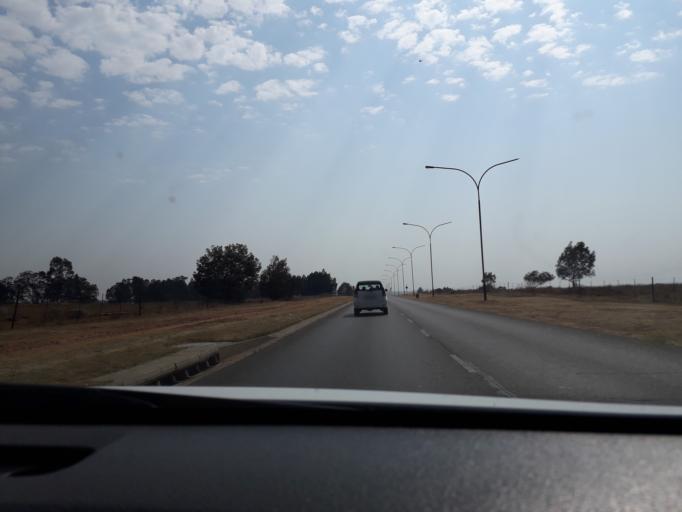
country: ZA
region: Gauteng
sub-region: Ekurhuleni Metropolitan Municipality
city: Tembisa
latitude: -26.0679
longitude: 28.2648
